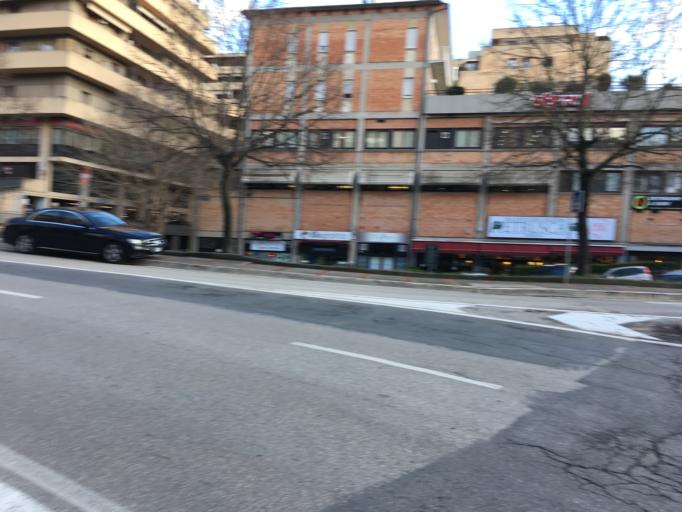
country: IT
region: Umbria
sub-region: Provincia di Perugia
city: Perugia
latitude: 43.1063
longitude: 12.3772
